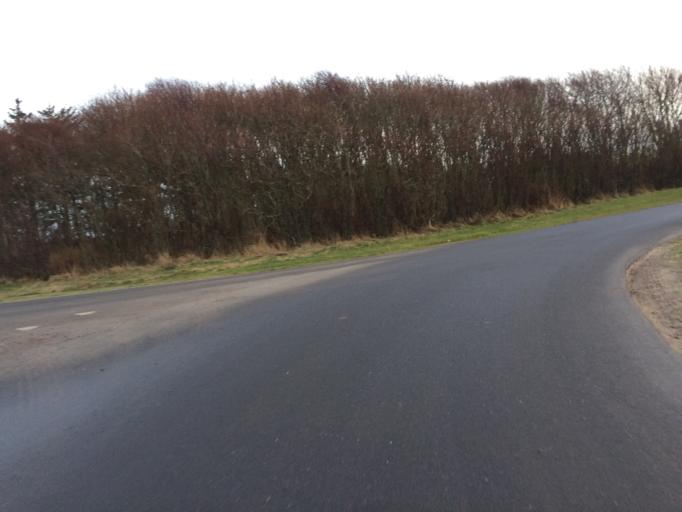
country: DK
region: Central Jutland
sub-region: Holstebro Kommune
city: Ulfborg
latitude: 56.2770
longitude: 8.2907
